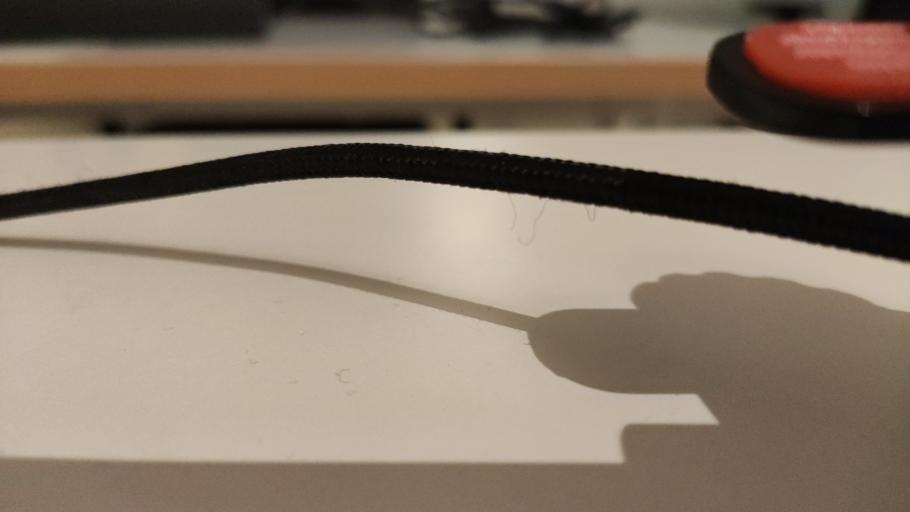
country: RU
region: Moskovskaya
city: Semkhoz
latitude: 56.3986
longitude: 38.0336
